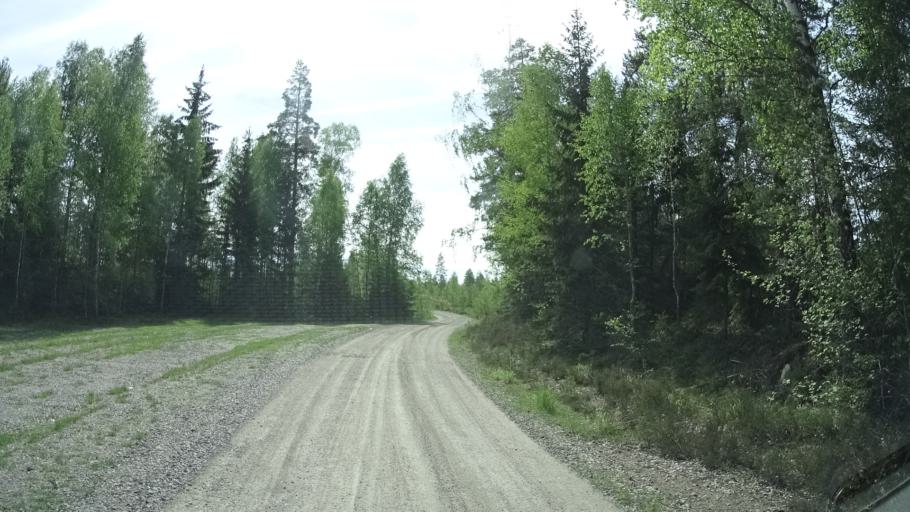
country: SE
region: OEstergoetland
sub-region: Finspangs Kommun
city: Finspang
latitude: 58.7743
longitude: 15.8432
